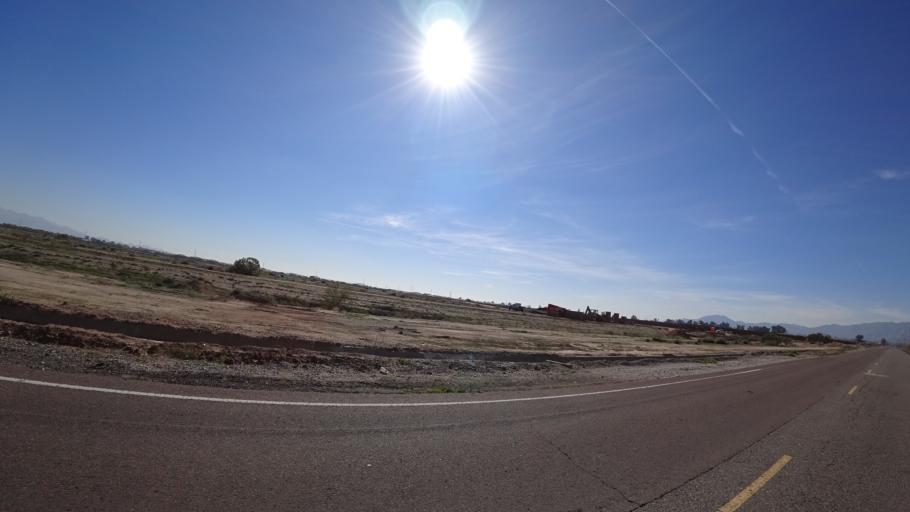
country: US
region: Arizona
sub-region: Maricopa County
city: Citrus Park
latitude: 33.5082
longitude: -112.4511
